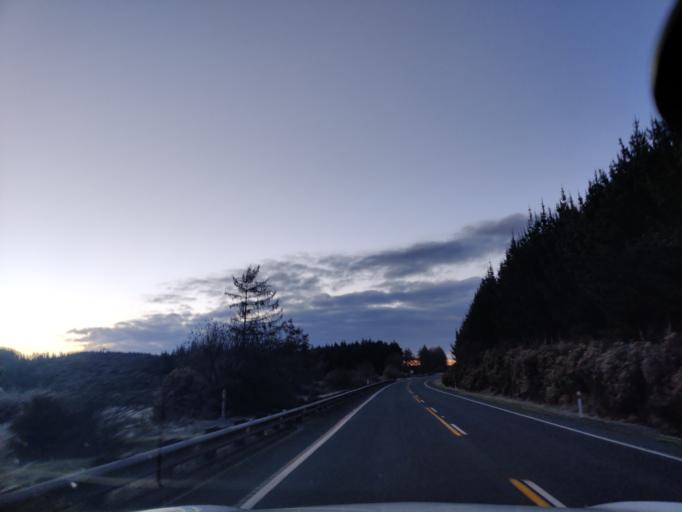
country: NZ
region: Waikato
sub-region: South Waikato District
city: Tokoroa
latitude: -38.3282
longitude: 175.9960
